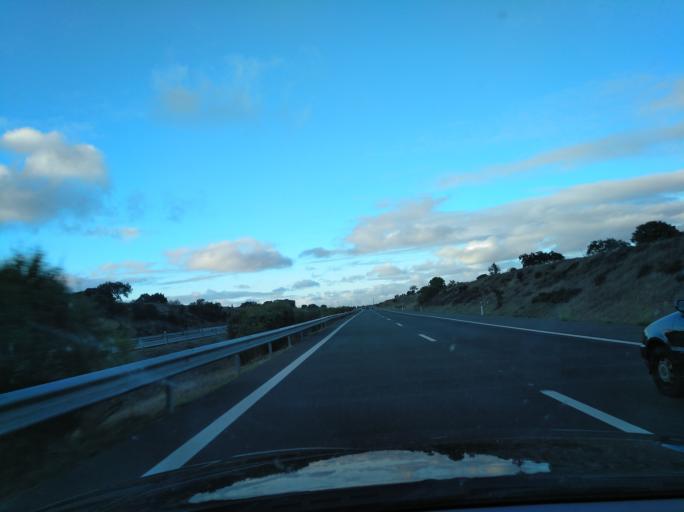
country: PT
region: Beja
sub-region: Aljustrel
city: Aljustrel
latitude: 37.9603
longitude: -8.2511
